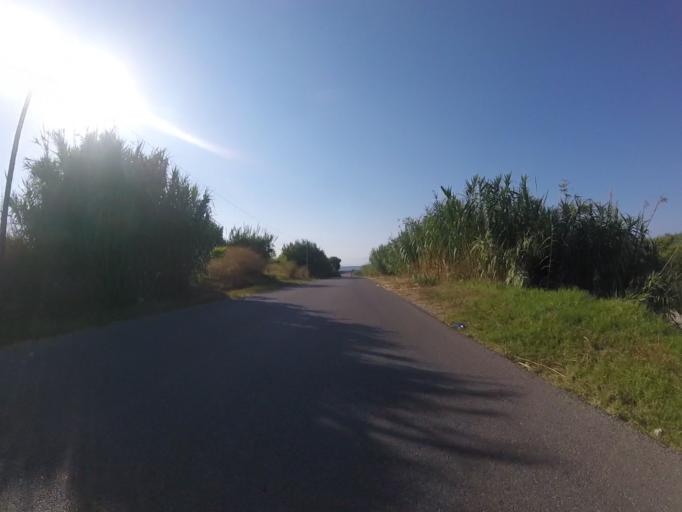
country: ES
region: Valencia
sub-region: Provincia de Castello
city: Benicarlo
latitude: 40.4209
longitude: 0.4357
